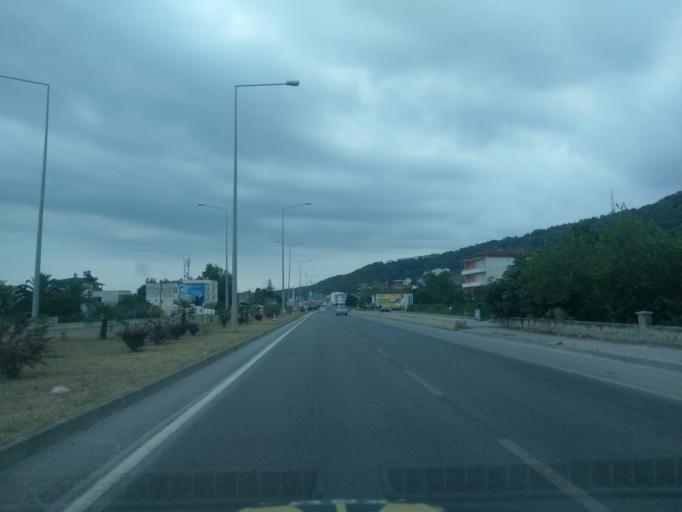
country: TR
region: Samsun
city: Taflan
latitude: 41.3912
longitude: 36.2018
